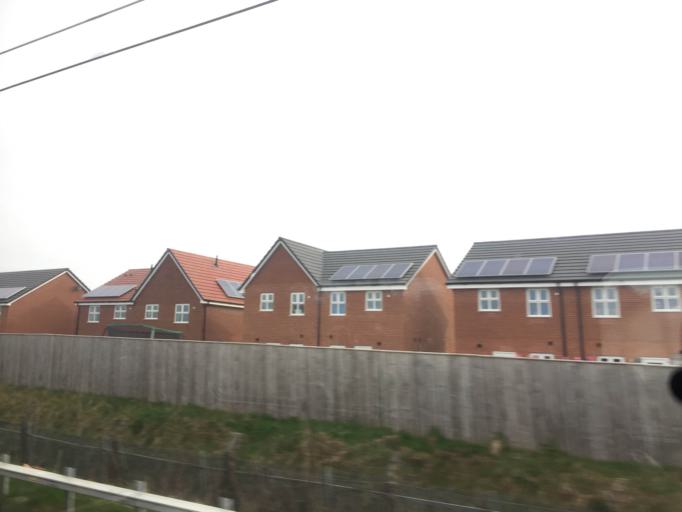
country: GB
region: England
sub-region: Lancashire
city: Coppull
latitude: 53.6192
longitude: -2.6573
